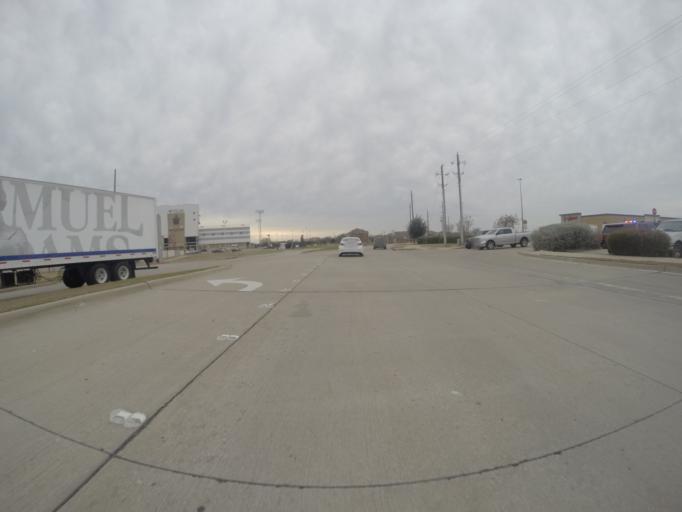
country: US
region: Texas
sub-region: Collin County
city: Saint Paul
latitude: 33.0379
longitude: -96.5686
